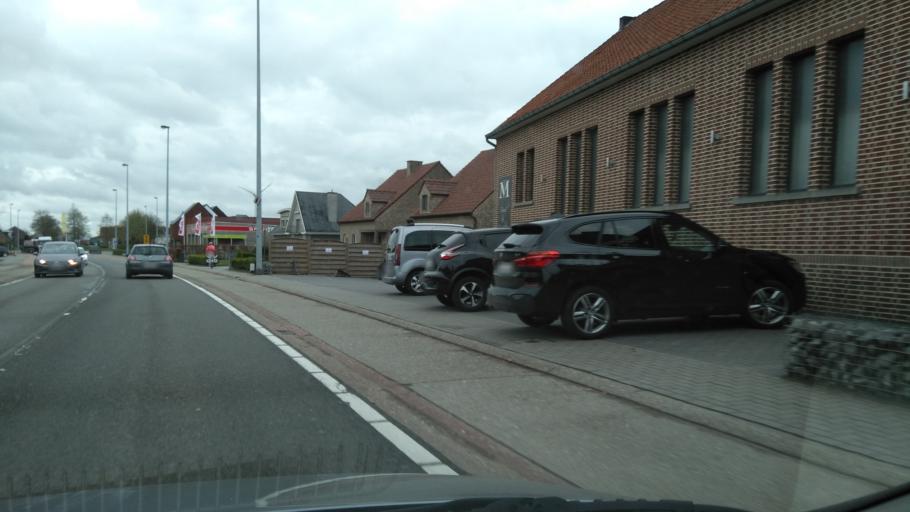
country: BE
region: Flanders
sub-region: Provincie Limburg
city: Bilzen
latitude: 50.8388
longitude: 5.5524
